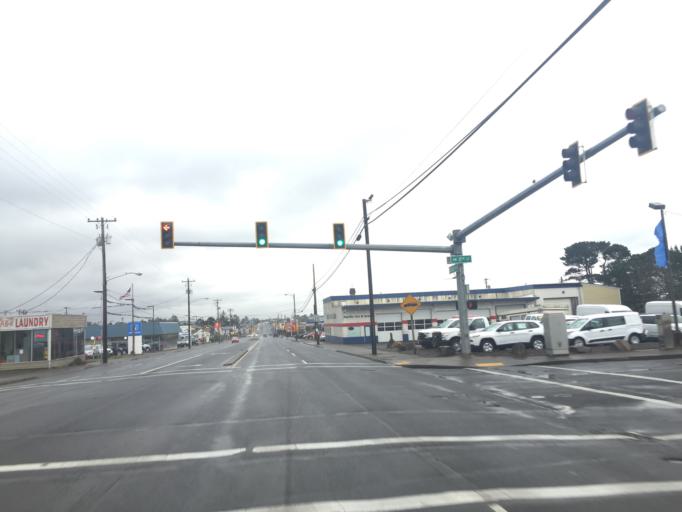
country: US
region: Oregon
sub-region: Lincoln County
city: Newport
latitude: 44.6449
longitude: -124.0531
